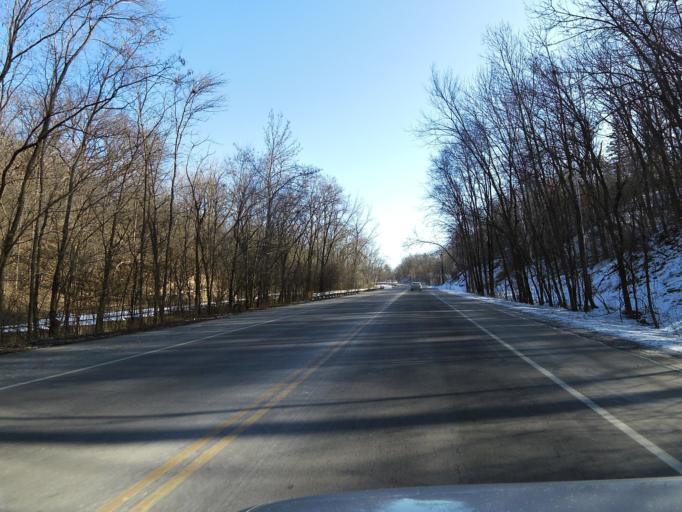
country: US
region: Minnesota
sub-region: Ramsey County
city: Maplewood
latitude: 44.9300
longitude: -93.0193
